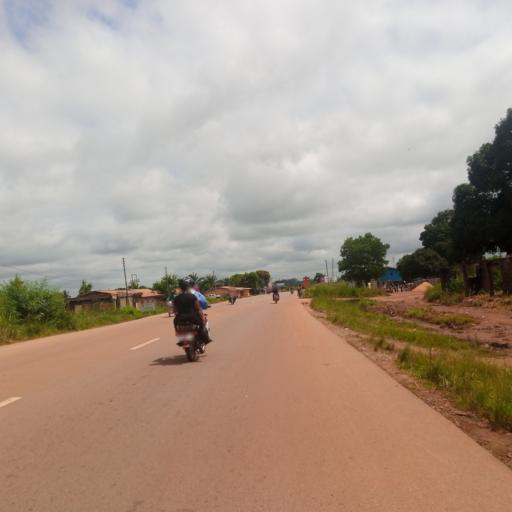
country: SL
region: Eastern Province
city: Kenema
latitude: 7.8977
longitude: -11.1760
